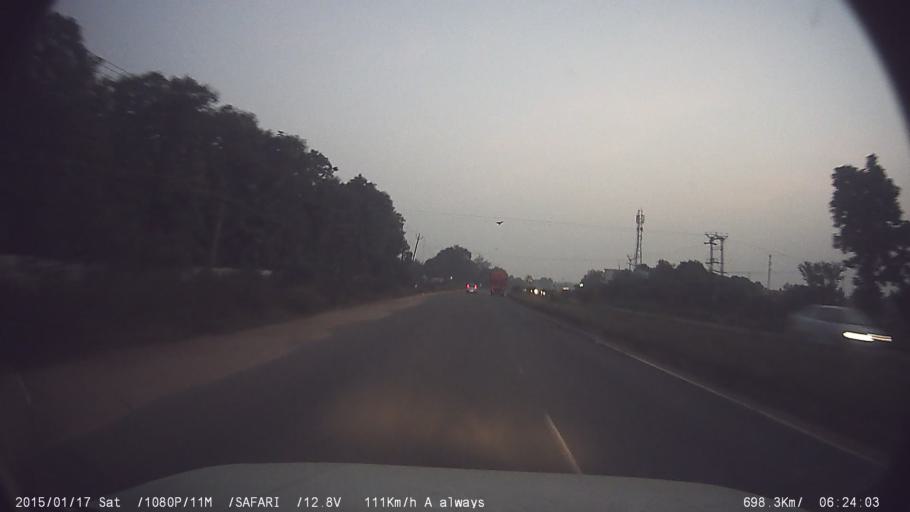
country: IN
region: Tamil Nadu
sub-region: Kancheepuram
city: Sriperumbudur
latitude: 12.9152
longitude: 79.8580
